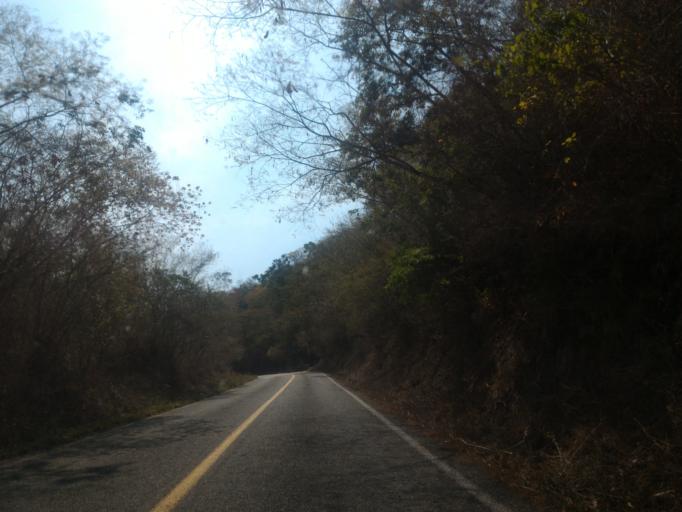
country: MX
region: Michoacan
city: Coahuayana Viejo
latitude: 18.3481
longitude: -103.4857
